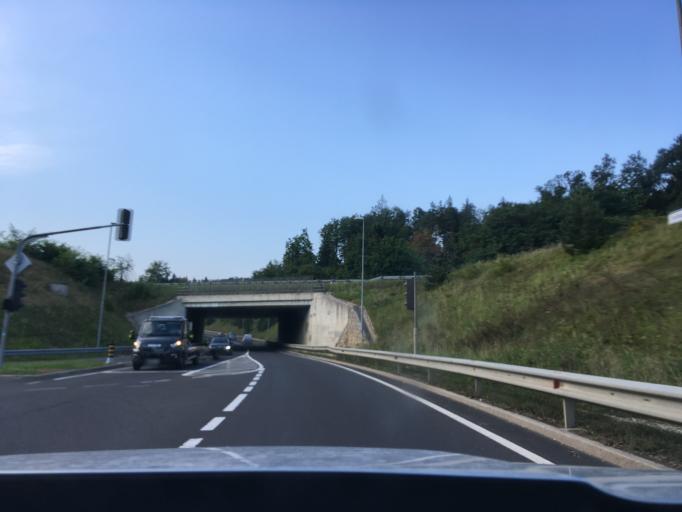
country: SI
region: Novo Mesto
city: Novo Mesto
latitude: 45.8285
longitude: 15.1807
